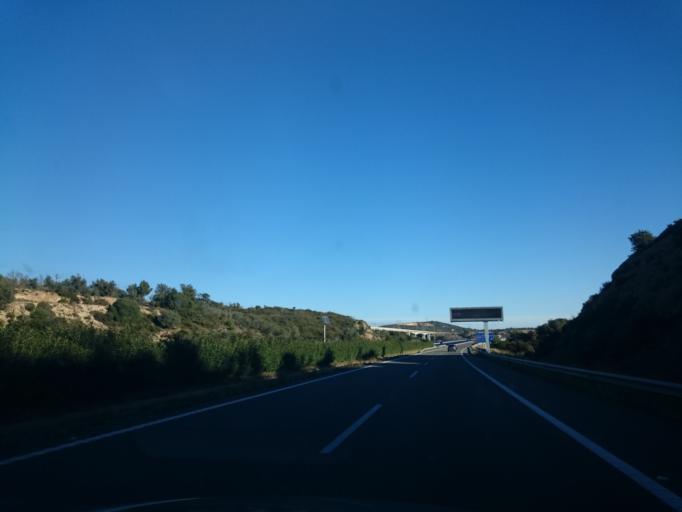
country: ES
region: Catalonia
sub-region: Provincia de Tarragona
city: Amposta
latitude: 40.7226
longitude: 0.5654
